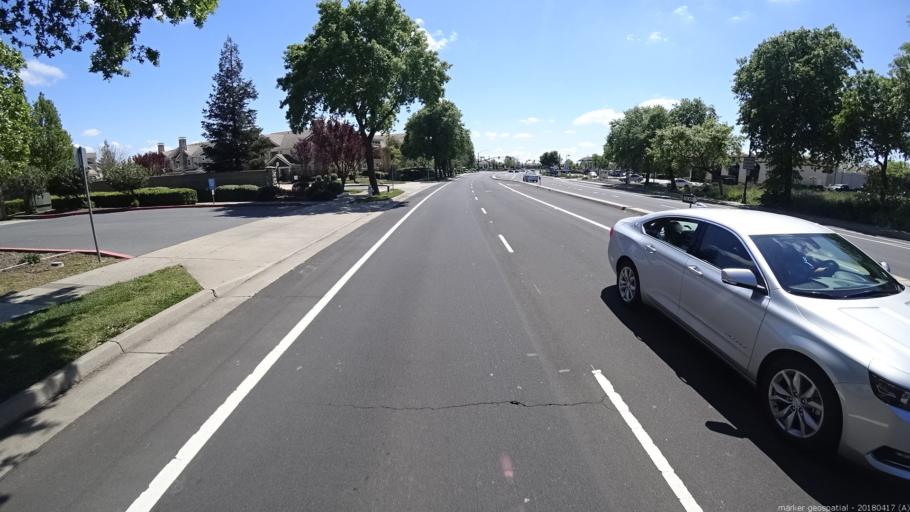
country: US
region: California
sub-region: Sacramento County
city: Laguna
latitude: 38.4101
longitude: -121.4770
